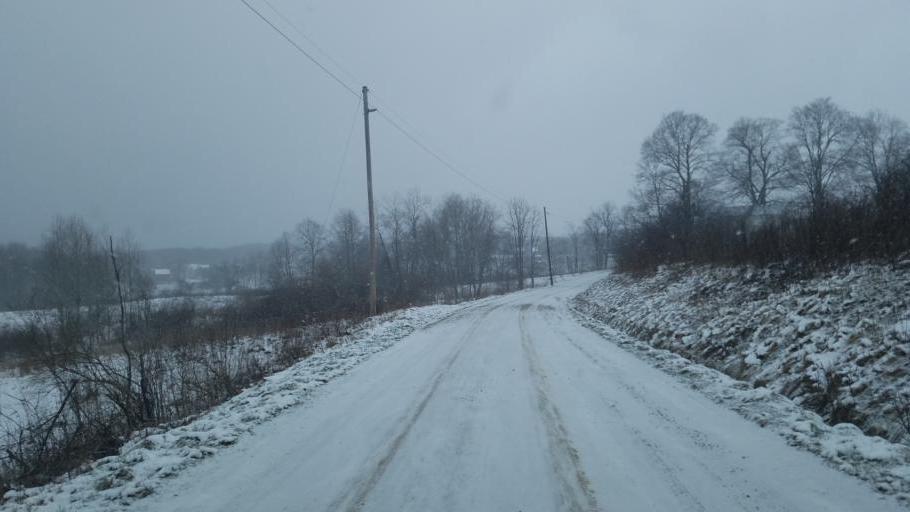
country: US
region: Pennsylvania
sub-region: Venango County
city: Sugarcreek
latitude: 41.4544
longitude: -79.9568
